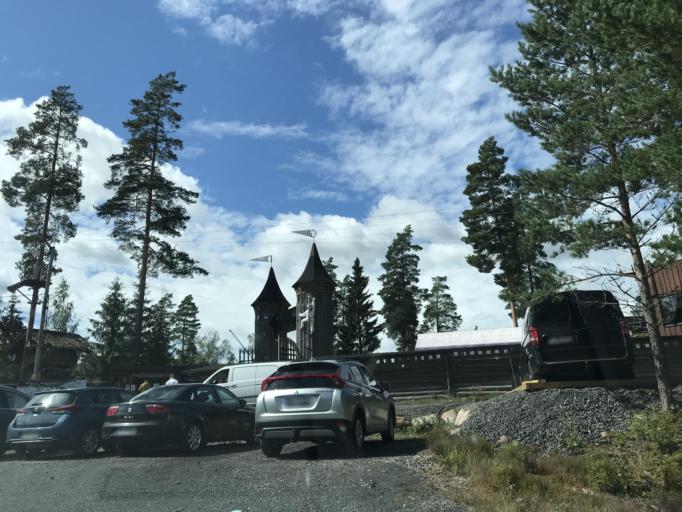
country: FI
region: Haeme
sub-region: Forssa
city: Tammela
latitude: 60.6306
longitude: 23.7552
